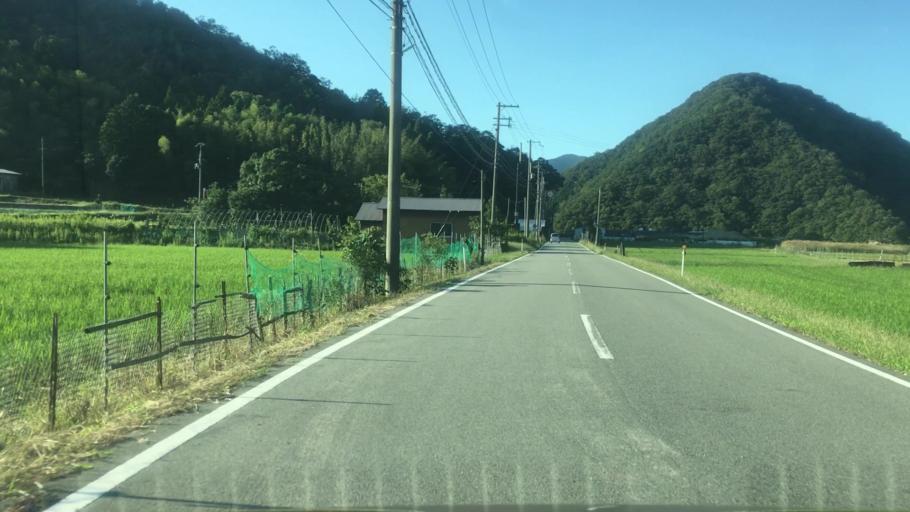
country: JP
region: Hyogo
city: Toyooka
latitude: 35.6124
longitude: 134.8282
